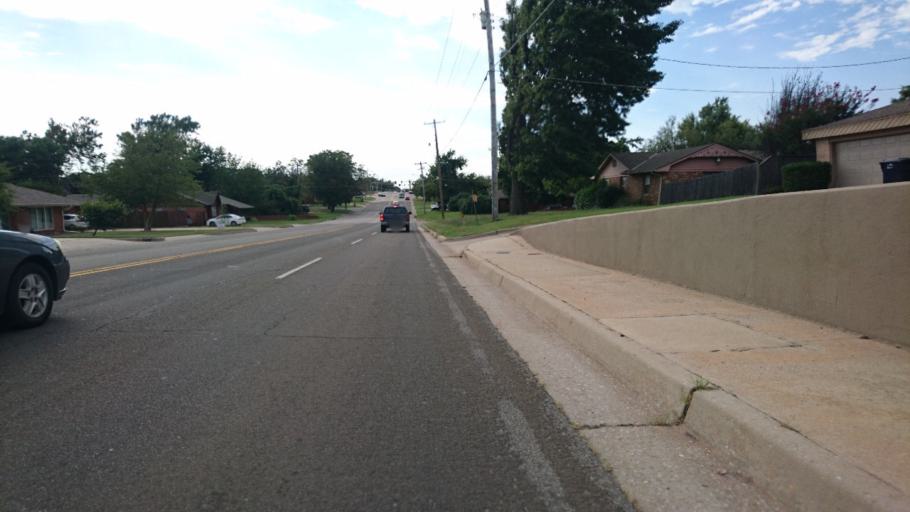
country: US
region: Oklahoma
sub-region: Oklahoma County
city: Warr Acres
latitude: 35.5077
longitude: -97.5723
